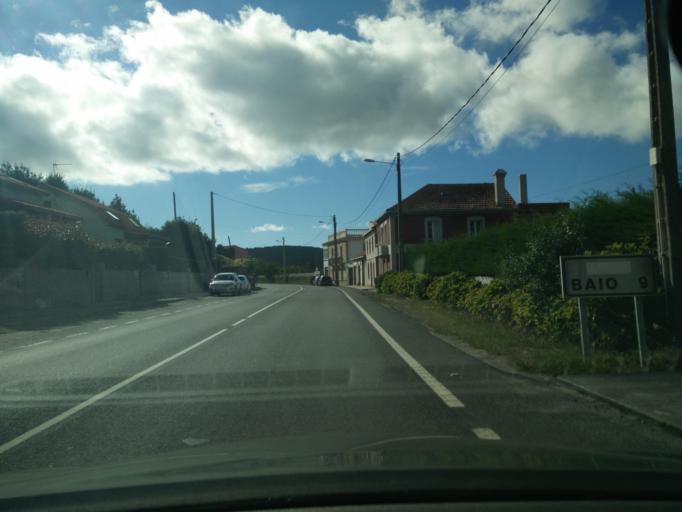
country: ES
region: Galicia
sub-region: Provincia da Coruna
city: Laxe
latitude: 43.2180
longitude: -8.9326
